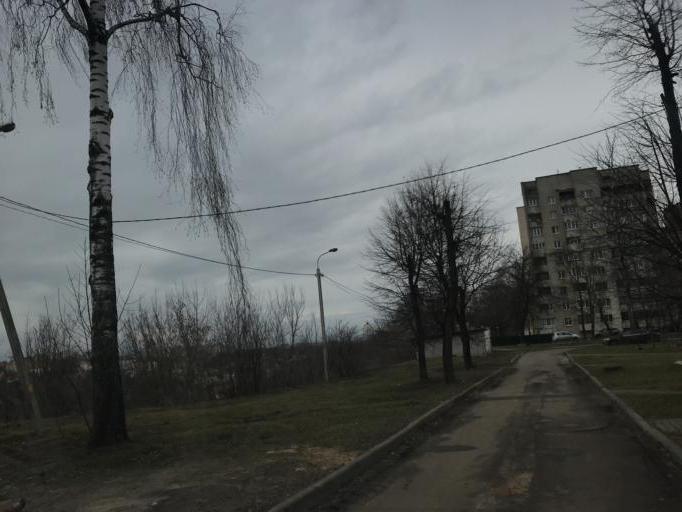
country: BY
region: Mogilev
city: Mahilyow
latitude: 53.8955
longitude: 30.3302
